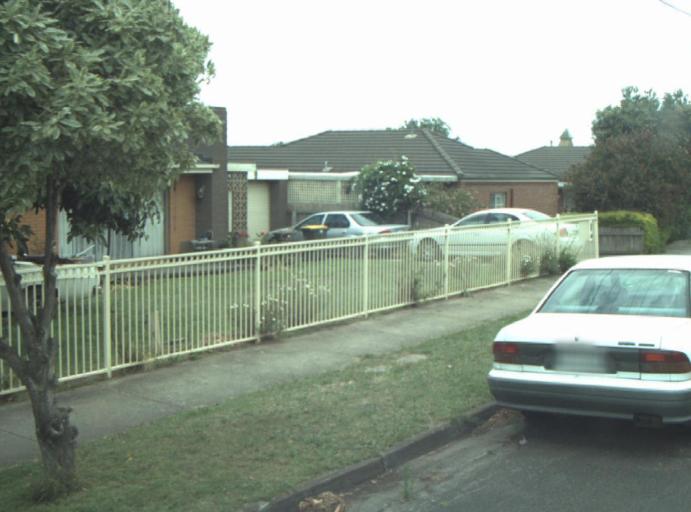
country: AU
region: Victoria
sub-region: Greater Geelong
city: Wandana Heights
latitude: -38.1827
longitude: 144.3109
